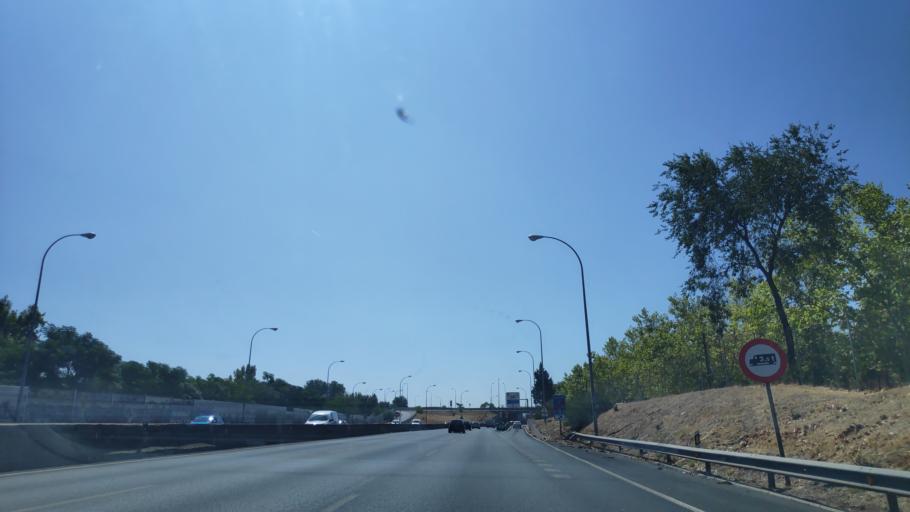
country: ES
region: Madrid
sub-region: Provincia de Madrid
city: Getafe
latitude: 40.2985
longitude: -3.7380
